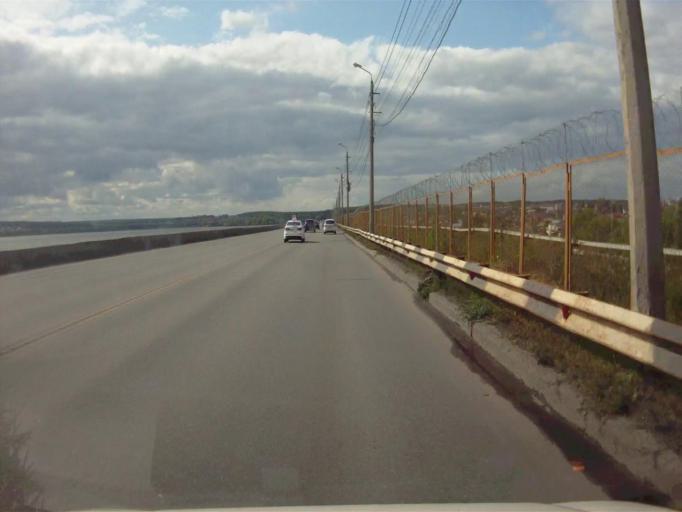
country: RU
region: Chelyabinsk
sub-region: Gorod Chelyabinsk
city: Chelyabinsk
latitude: 55.1458
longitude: 61.3215
